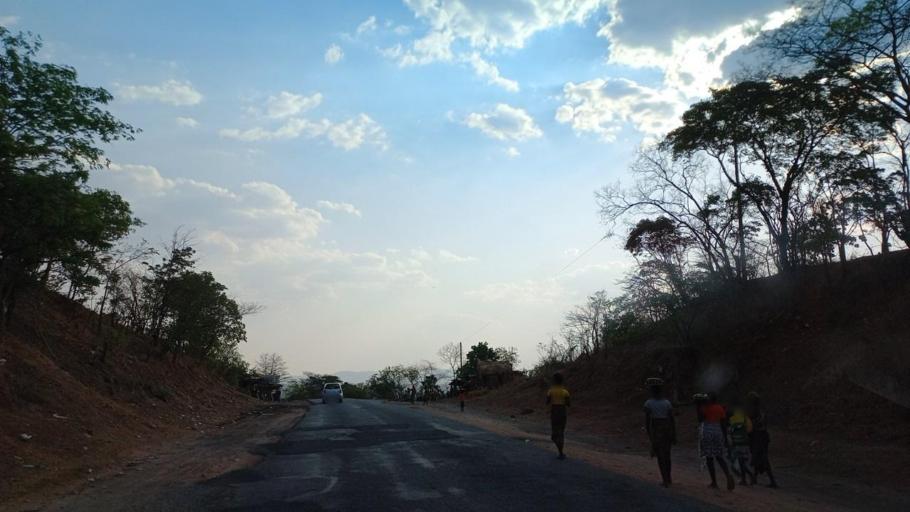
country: ZM
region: Lusaka
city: Luangwa
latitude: -15.0186
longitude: 29.9546
